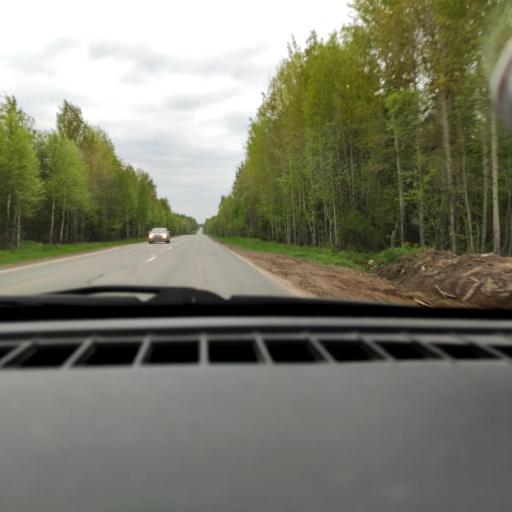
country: RU
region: Perm
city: Polazna
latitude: 58.2715
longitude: 56.1669
